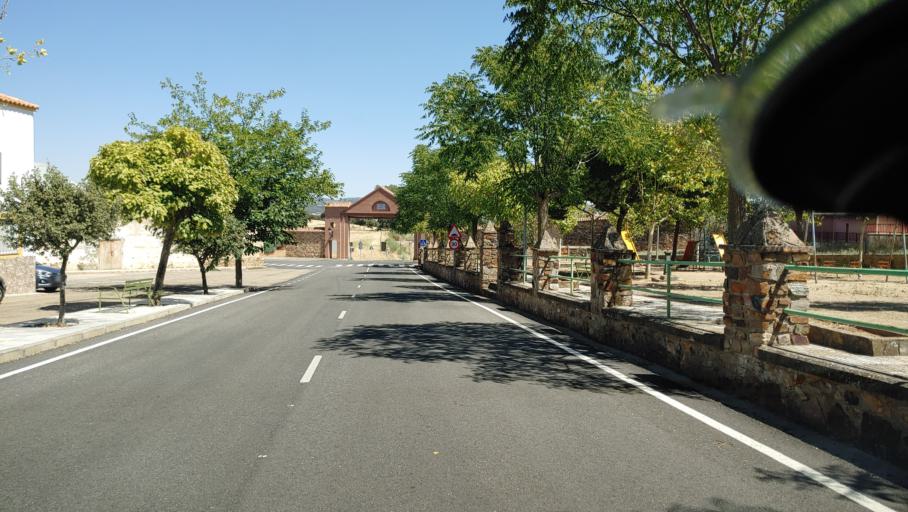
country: ES
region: Castille-La Mancha
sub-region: Provincia de Ciudad Real
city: Alamillo
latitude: 38.7384
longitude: -4.7082
